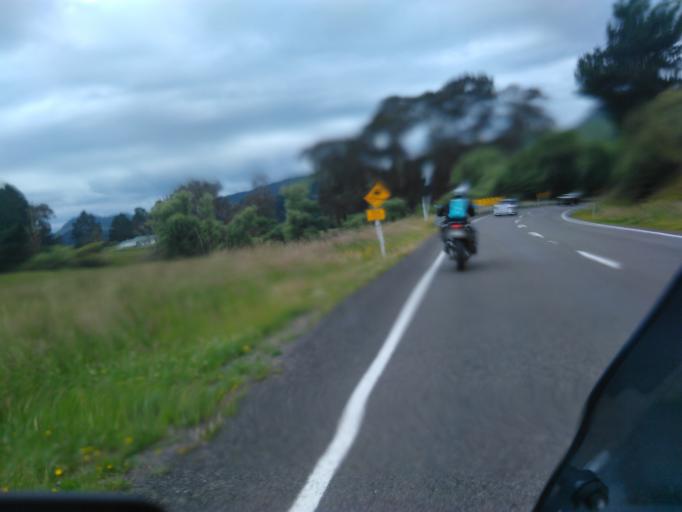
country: NZ
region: Bay of Plenty
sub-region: Opotiki District
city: Opotiki
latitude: -38.3593
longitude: 177.5274
